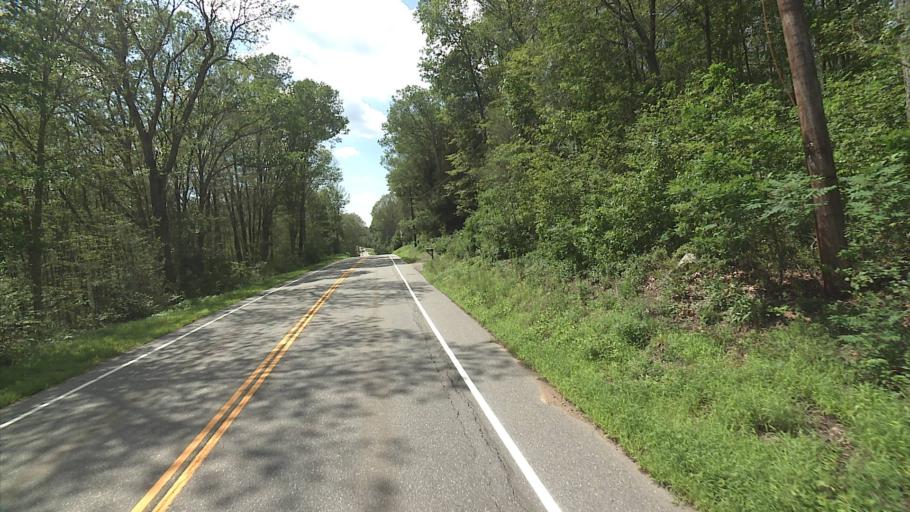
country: US
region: Connecticut
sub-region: Windham County
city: Windham
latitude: 41.8318
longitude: -72.0966
